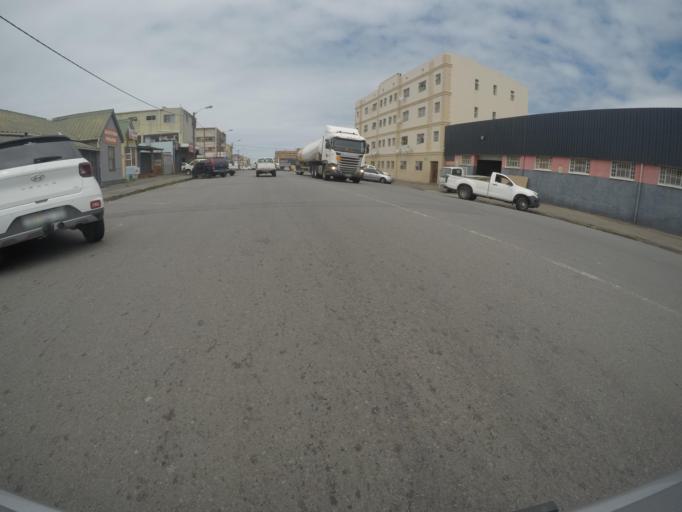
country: ZA
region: Eastern Cape
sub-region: Buffalo City Metropolitan Municipality
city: East London
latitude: -33.0148
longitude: 27.9122
